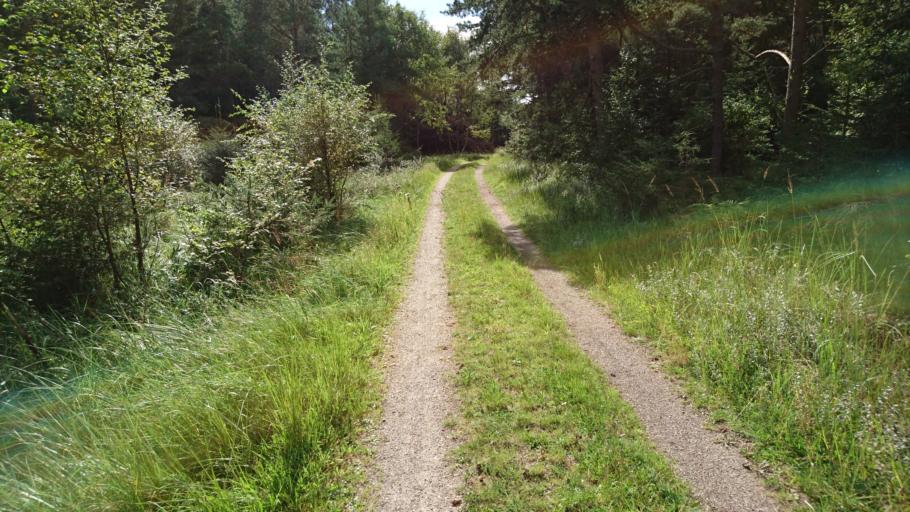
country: DK
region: North Denmark
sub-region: Frederikshavn Kommune
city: Skagen
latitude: 57.7109
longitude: 10.5129
